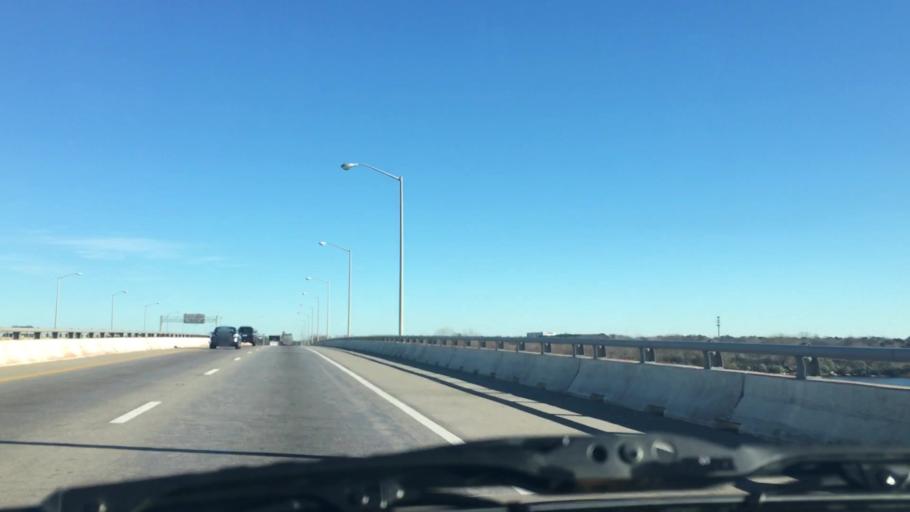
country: US
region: Virginia
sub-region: City of Hampton
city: East Hampton
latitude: 36.9630
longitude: -76.2747
